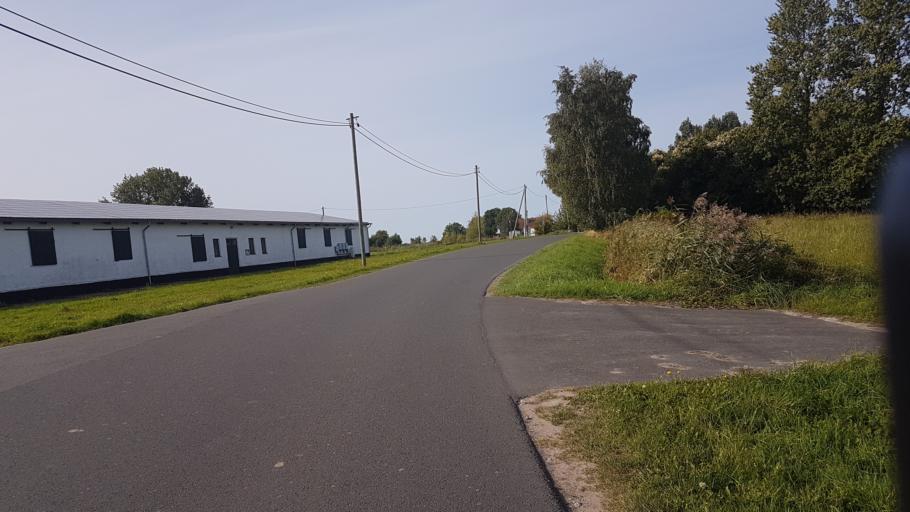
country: DE
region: Mecklenburg-Vorpommern
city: Gingst
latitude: 54.4506
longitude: 13.1462
